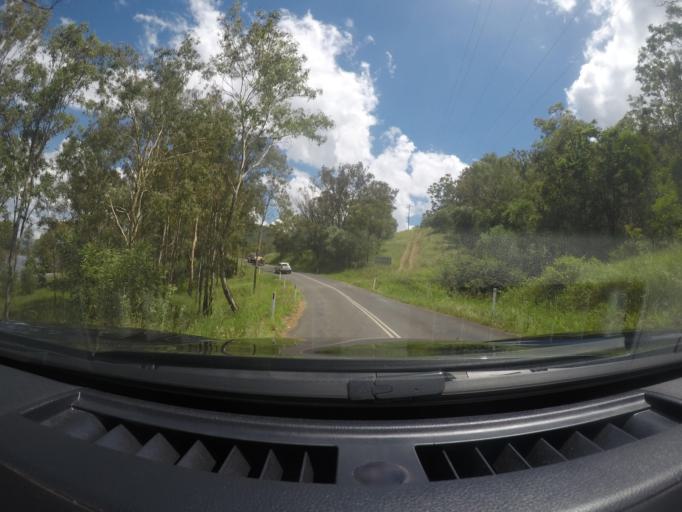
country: AU
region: Queensland
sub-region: Moreton Bay
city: Woodford
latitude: -27.1045
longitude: 152.5603
